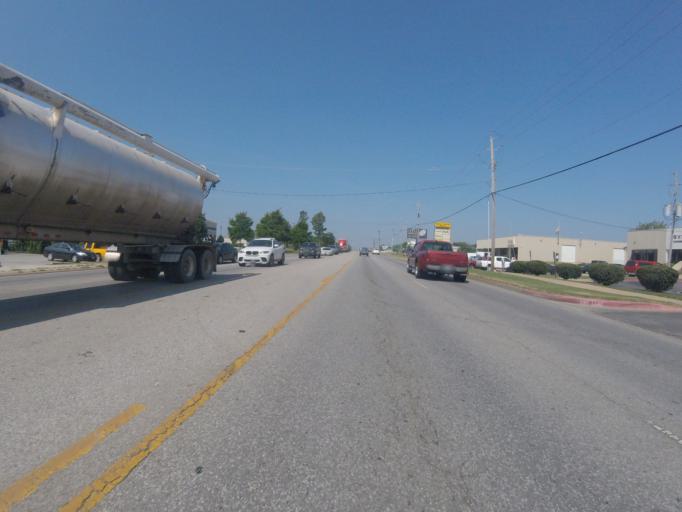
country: US
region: Arkansas
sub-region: Washington County
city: Springdale
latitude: 36.1671
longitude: -94.1266
